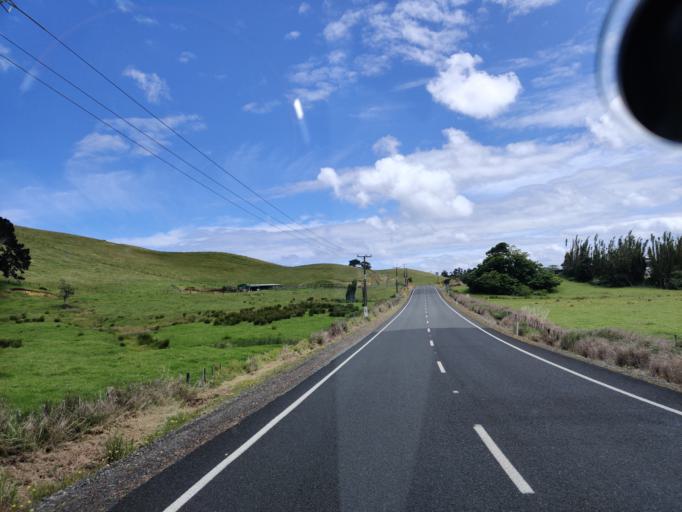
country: NZ
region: Northland
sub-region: Far North District
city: Kaitaia
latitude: -34.9574
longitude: 173.1912
